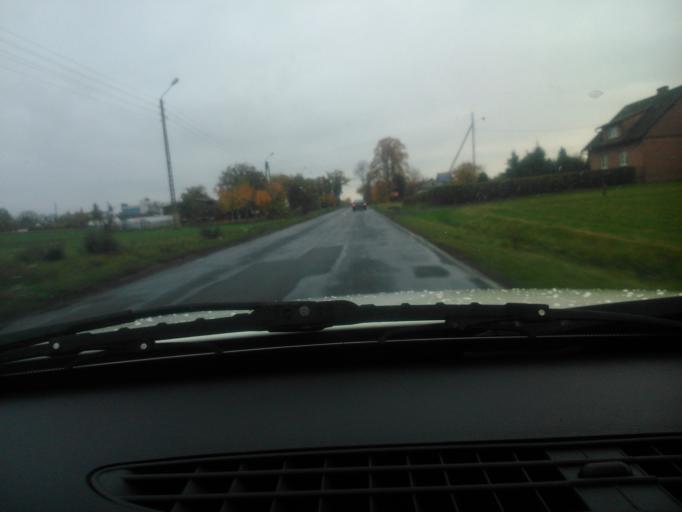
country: PL
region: Kujawsko-Pomorskie
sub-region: Powiat golubsko-dobrzynski
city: Golub-Dobrzyn
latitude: 53.1237
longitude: 19.0370
